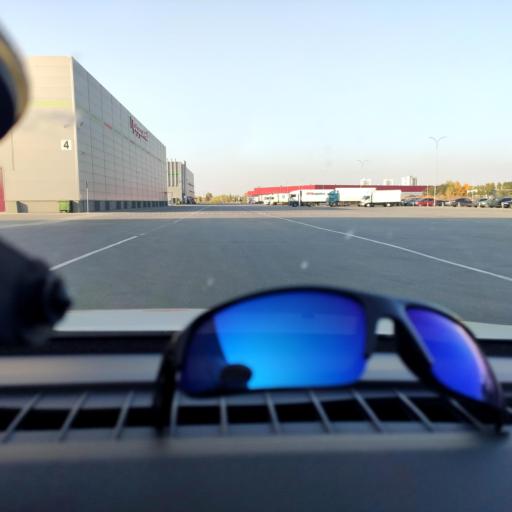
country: RU
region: Samara
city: Samara
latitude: 53.0946
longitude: 50.1342
